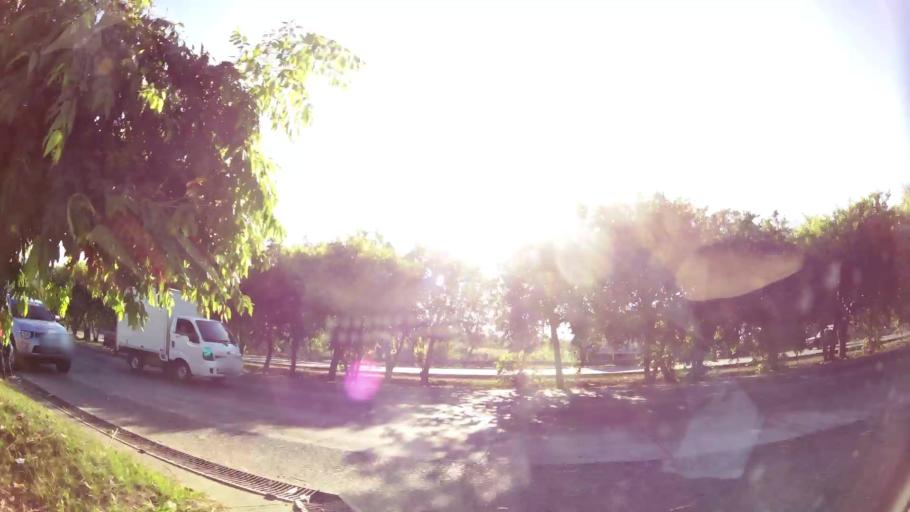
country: SV
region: La Libertad
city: Santa Tecla
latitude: 13.7359
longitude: -89.3606
